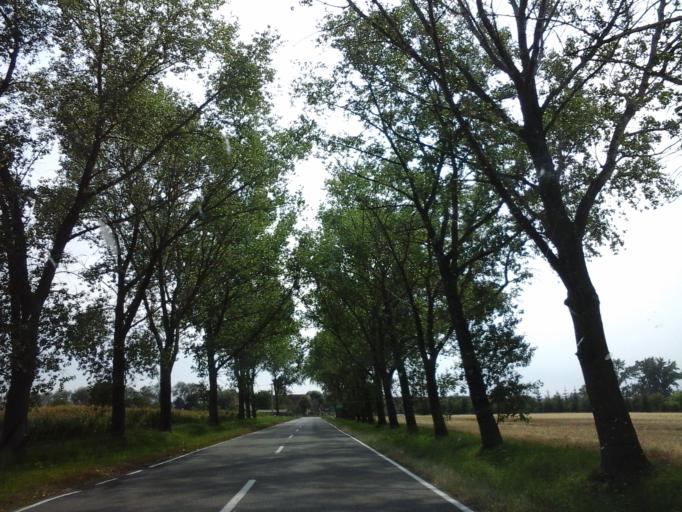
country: PL
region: Lower Silesian Voivodeship
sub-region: Powiat strzelinski
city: Strzelin
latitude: 50.8528
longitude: 17.0600
